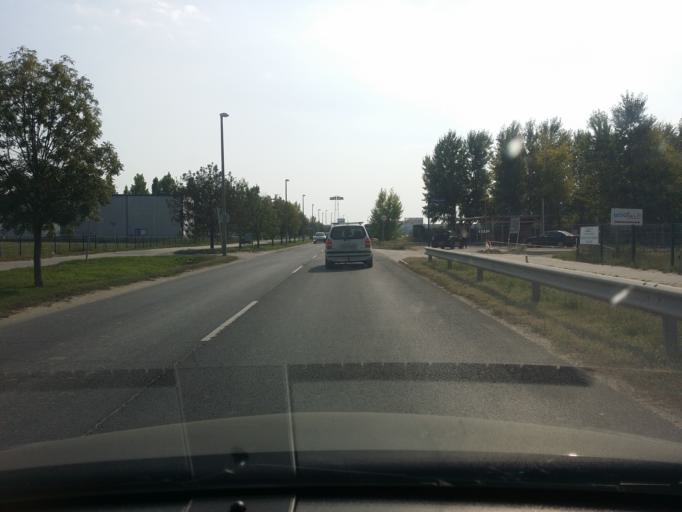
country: HU
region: Pest
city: Dunakeszi
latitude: 47.6153
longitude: 19.1183
